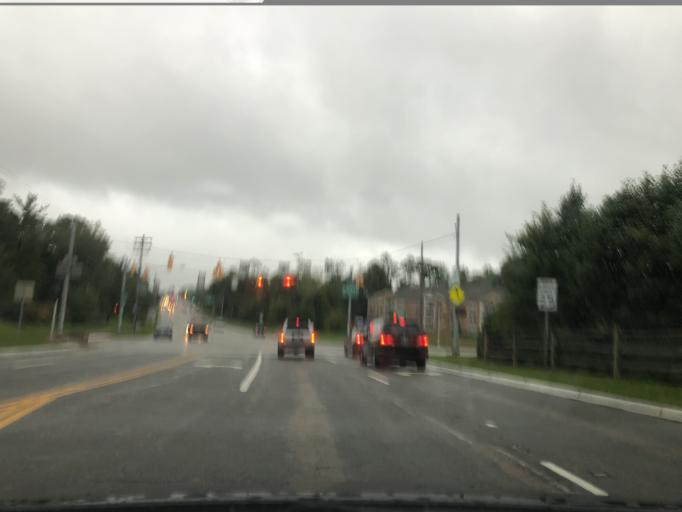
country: US
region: Ohio
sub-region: Hamilton County
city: Dillonvale
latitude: 39.2315
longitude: -84.3948
